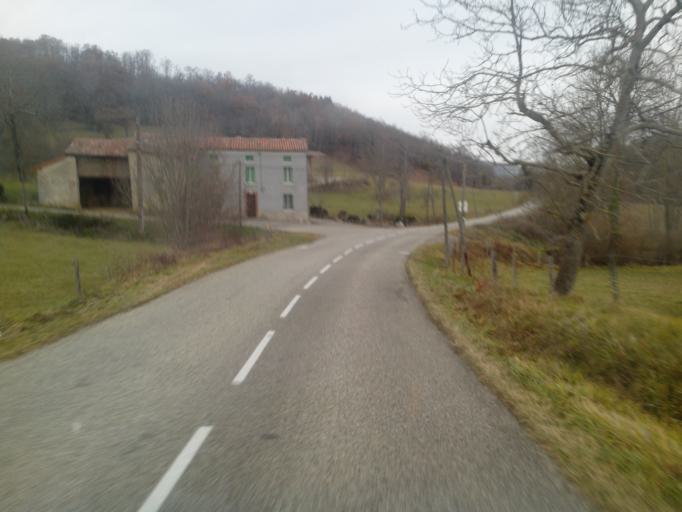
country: FR
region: Midi-Pyrenees
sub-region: Departement de l'Ariege
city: Foix
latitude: 43.0184
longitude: 1.5296
